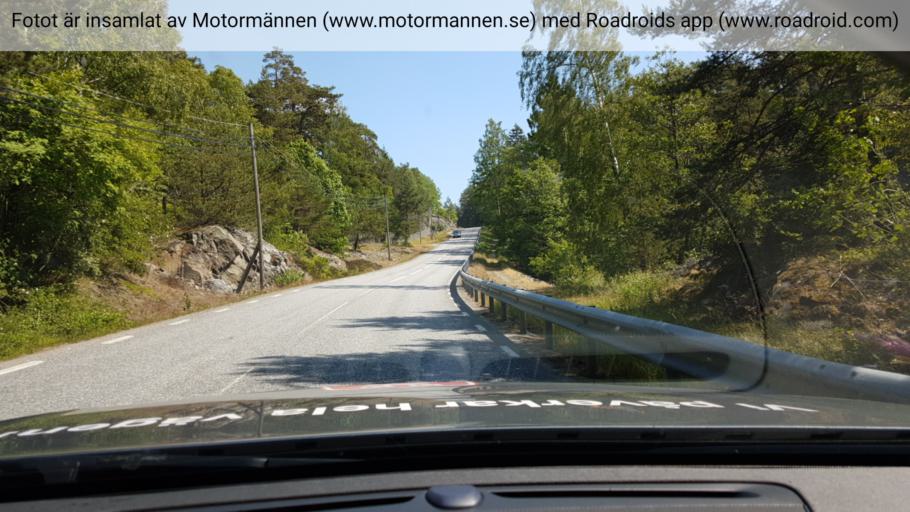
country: SE
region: Stockholm
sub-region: Nynashamns Kommun
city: Nynashamn
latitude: 58.9733
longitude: 18.0685
